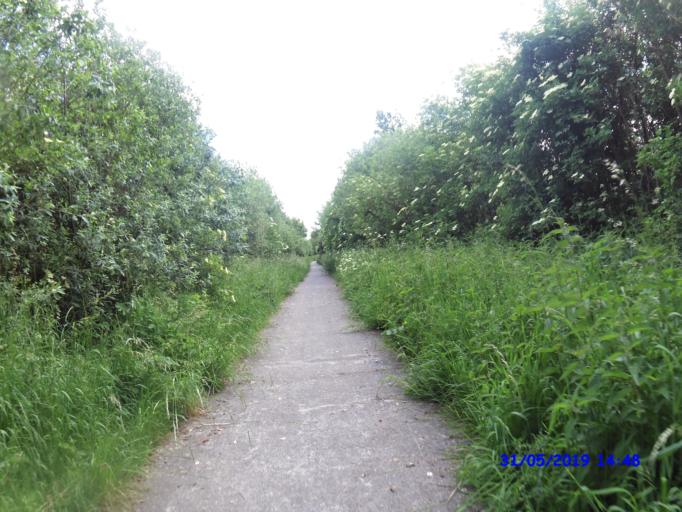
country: FR
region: Nord-Pas-de-Calais
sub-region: Departement du Nord
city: Comines
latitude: 50.7929
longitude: 2.9595
